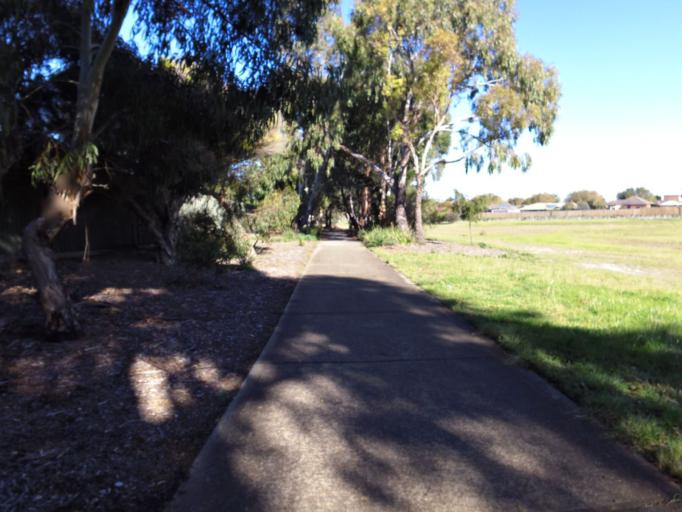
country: AU
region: Victoria
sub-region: Wyndham
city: Tarneit
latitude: -37.8734
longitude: 144.6739
